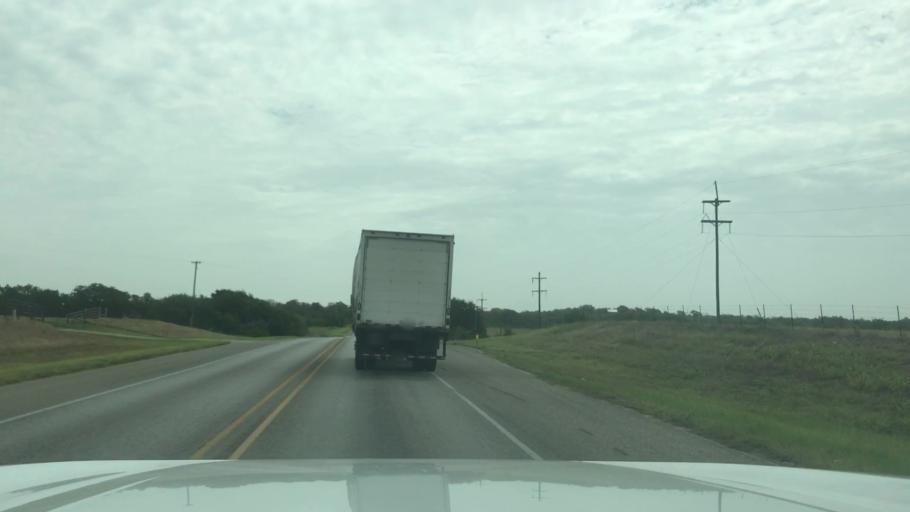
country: US
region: Texas
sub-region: Comanche County
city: De Leon
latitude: 32.0916
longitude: -98.4435
